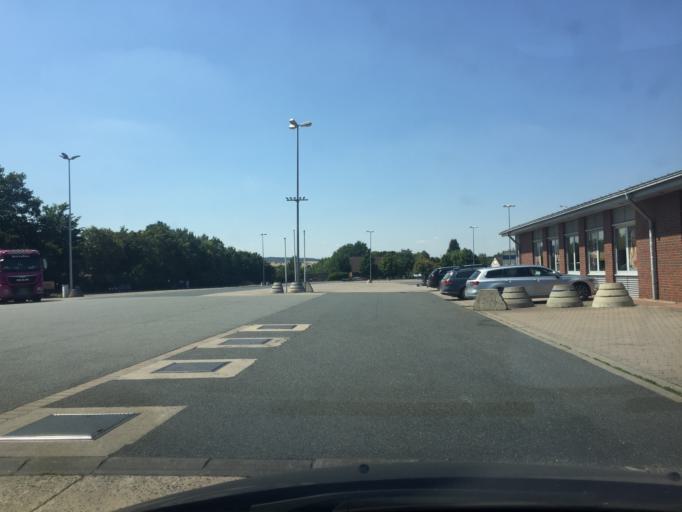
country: DE
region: Lower Saxony
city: Bockenem
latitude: 52.0019
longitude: 10.1345
